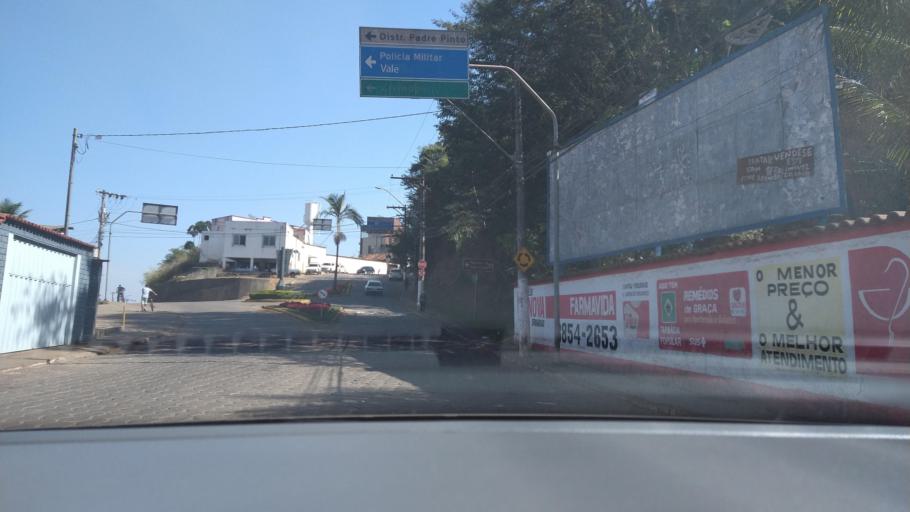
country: BR
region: Minas Gerais
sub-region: Rio Piracicaba
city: Rio Piracicaba
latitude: -19.9281
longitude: -43.1697
